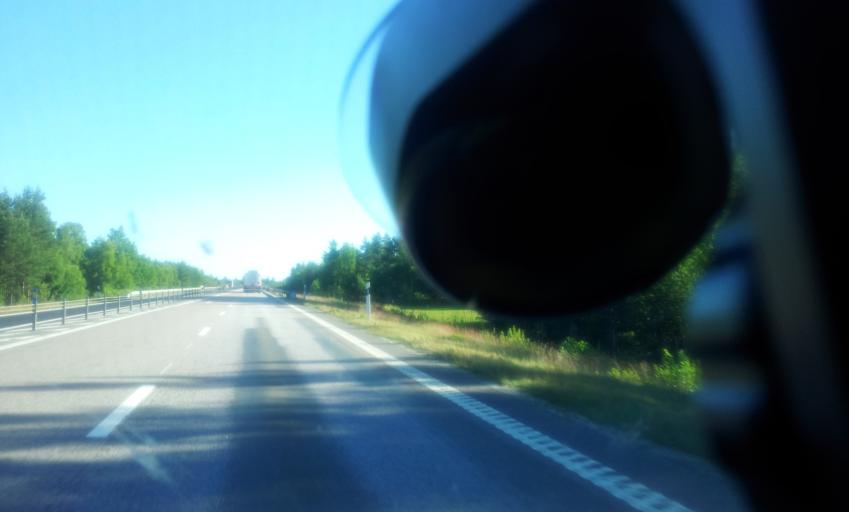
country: SE
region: Kalmar
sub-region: Torsas Kommun
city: Torsas
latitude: 56.4769
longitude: 16.0810
